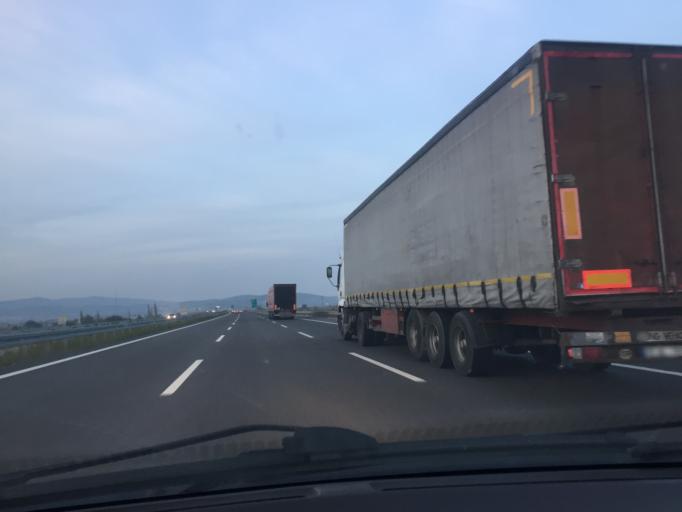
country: TR
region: Manisa
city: Halitpasa
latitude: 38.7509
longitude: 27.6599
